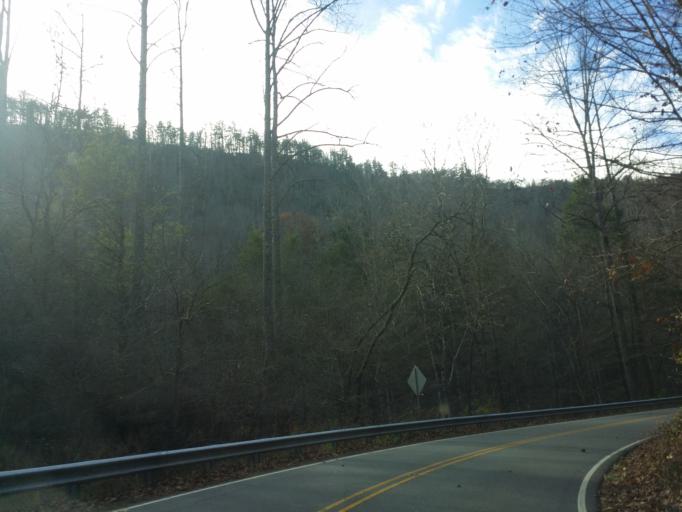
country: US
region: North Carolina
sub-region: McDowell County
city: West Marion
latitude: 35.7375
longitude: -82.1348
